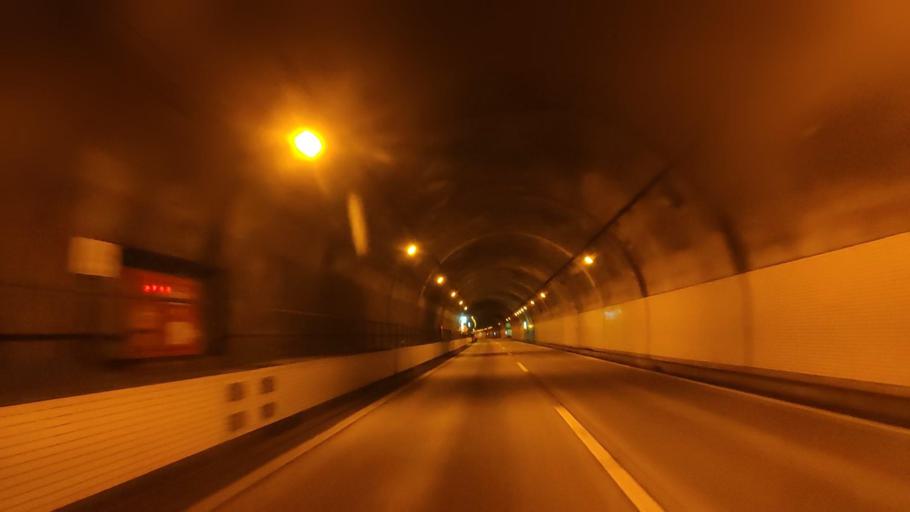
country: JP
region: Toyama
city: Nyuzen
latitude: 36.9757
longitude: 137.6522
